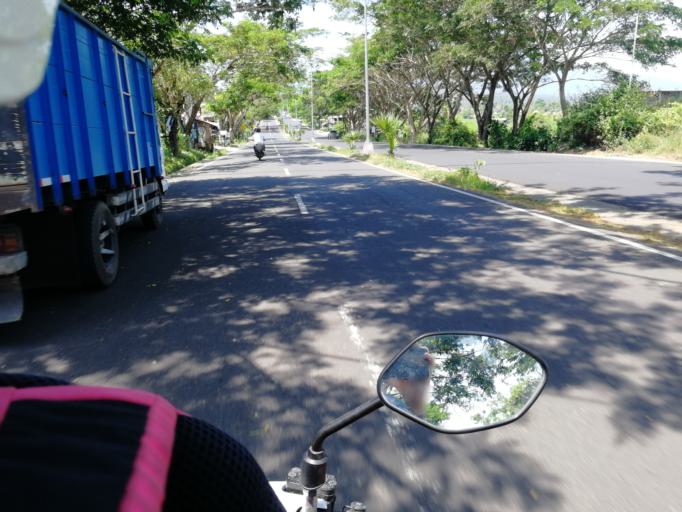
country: ID
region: Bali
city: Banjar Beji
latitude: -8.4450
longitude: 115.5891
